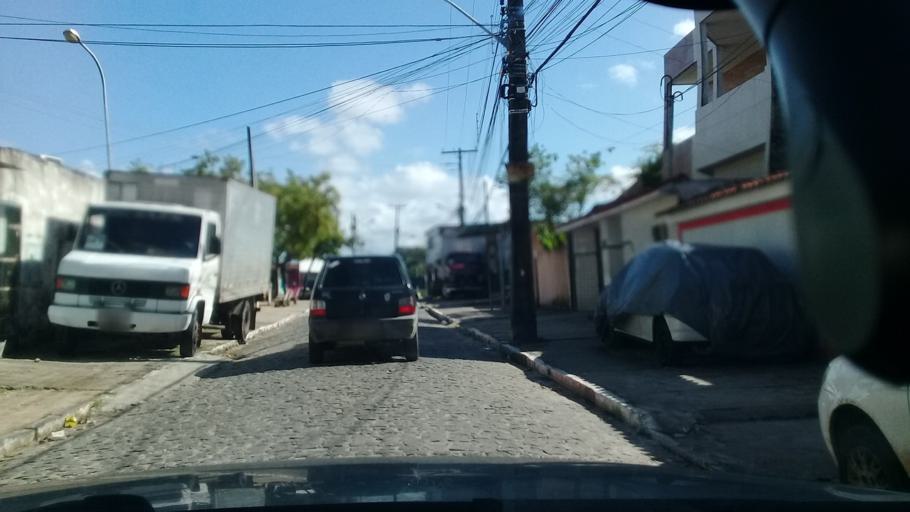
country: BR
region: Pernambuco
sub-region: Jaboatao Dos Guararapes
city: Jaboatao dos Guararapes
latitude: -8.1243
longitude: -34.9538
